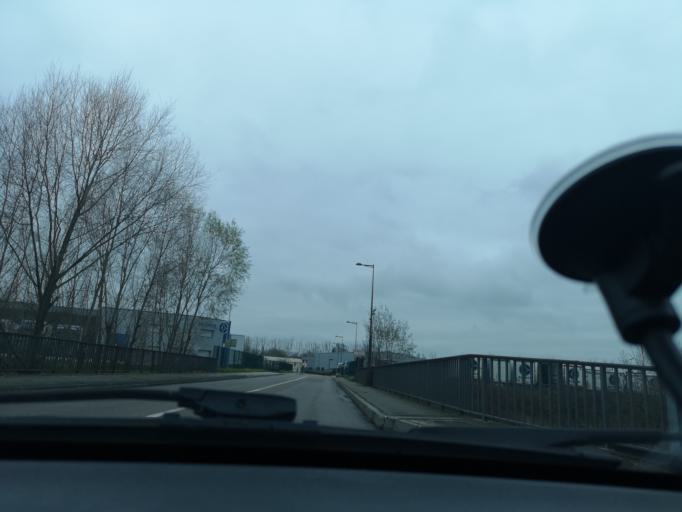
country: FR
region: Bourgogne
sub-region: Departement de Saone-et-Loire
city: Chatenoy-le-Royal
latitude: 46.7978
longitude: 4.8325
